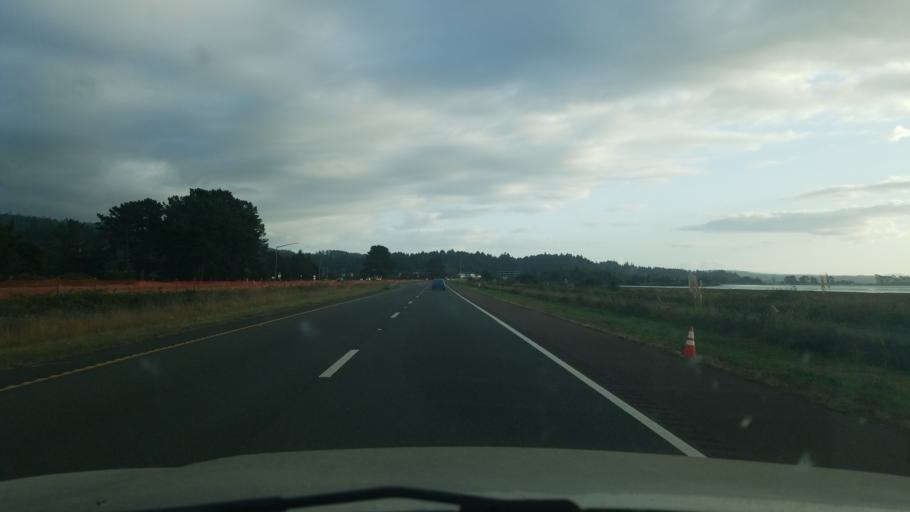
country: US
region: California
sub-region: Humboldt County
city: Bayside
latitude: 40.8373
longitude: -124.0822
